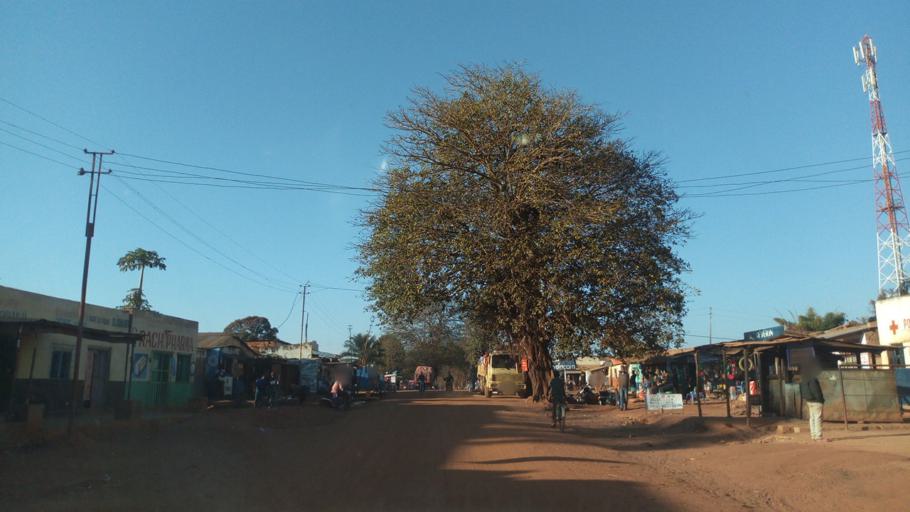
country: ZM
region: Luapula
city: Mwense
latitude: -10.3947
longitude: 28.6167
